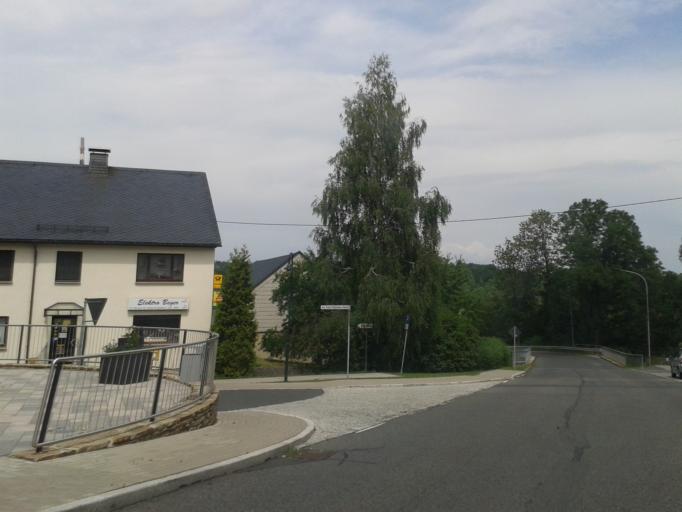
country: DE
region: Saxony
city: Halsbrucke
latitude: 50.9545
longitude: 13.3535
